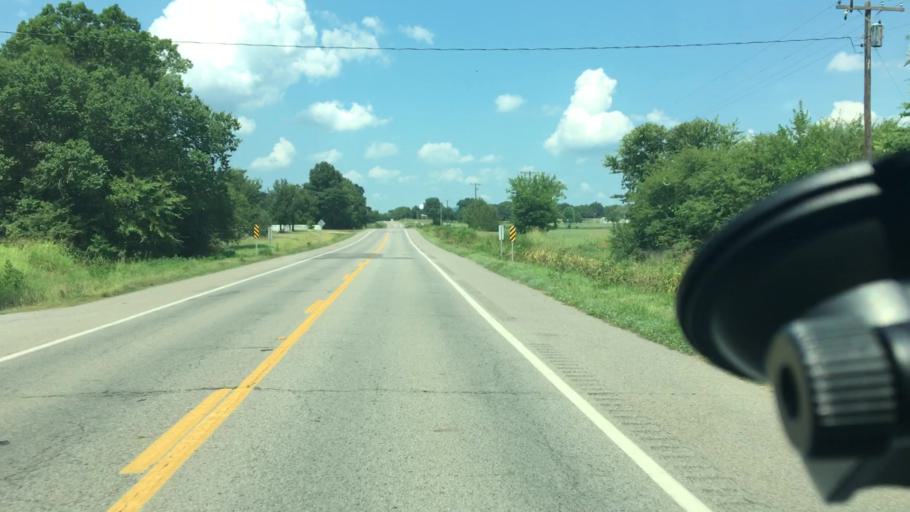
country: US
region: Arkansas
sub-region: Logan County
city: Paris
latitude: 35.2951
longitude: -93.6789
